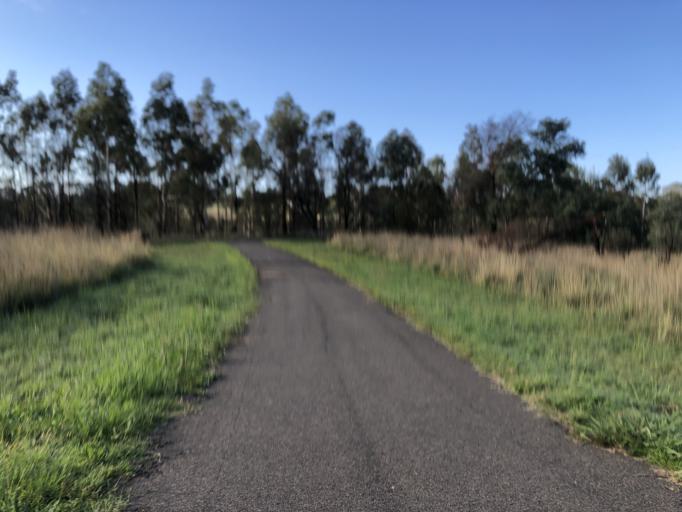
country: AU
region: New South Wales
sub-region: Orange Municipality
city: Orange
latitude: -33.3287
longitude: 149.0847
